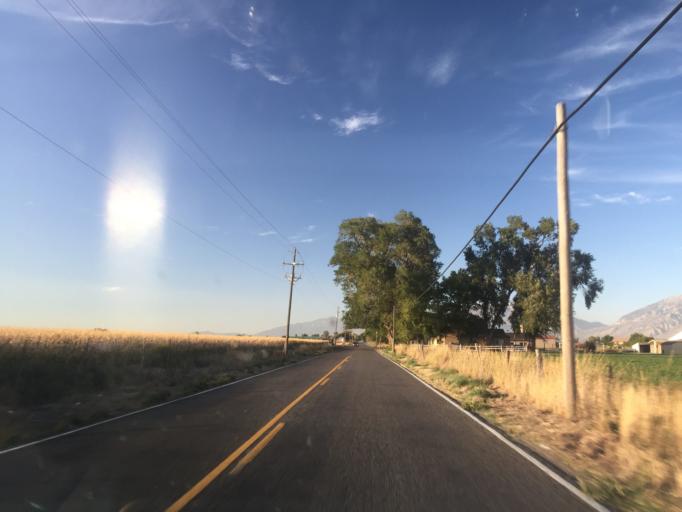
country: US
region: Utah
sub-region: Utah County
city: Benjamin
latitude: 40.1016
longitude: -111.7305
